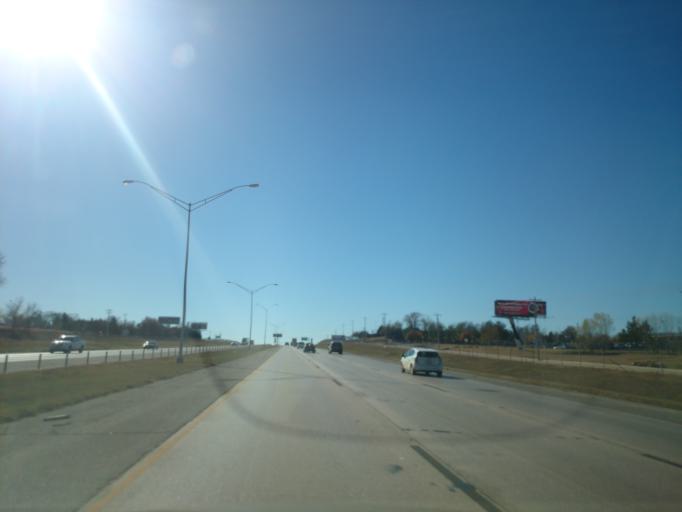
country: US
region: Oklahoma
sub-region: Oklahoma County
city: Edmond
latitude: 35.5749
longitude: -97.4456
